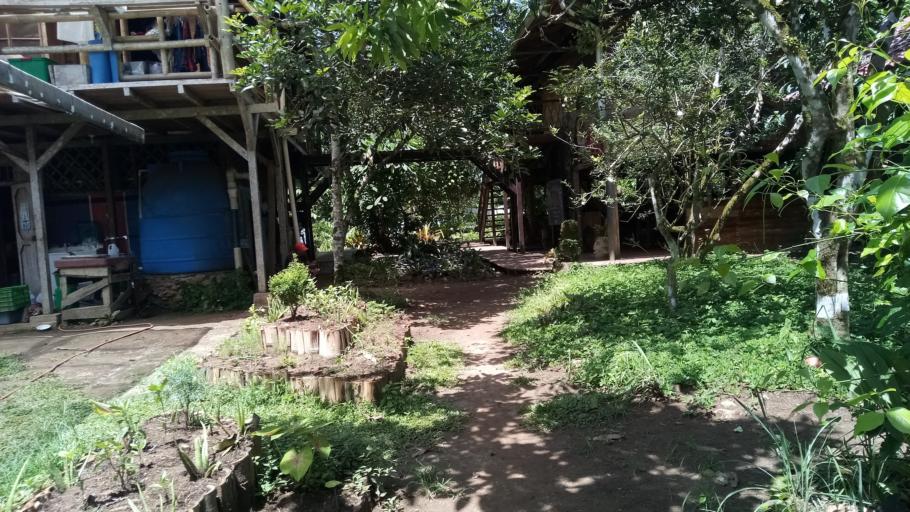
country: CR
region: Limon
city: Sixaola
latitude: 9.6239
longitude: -82.6201
